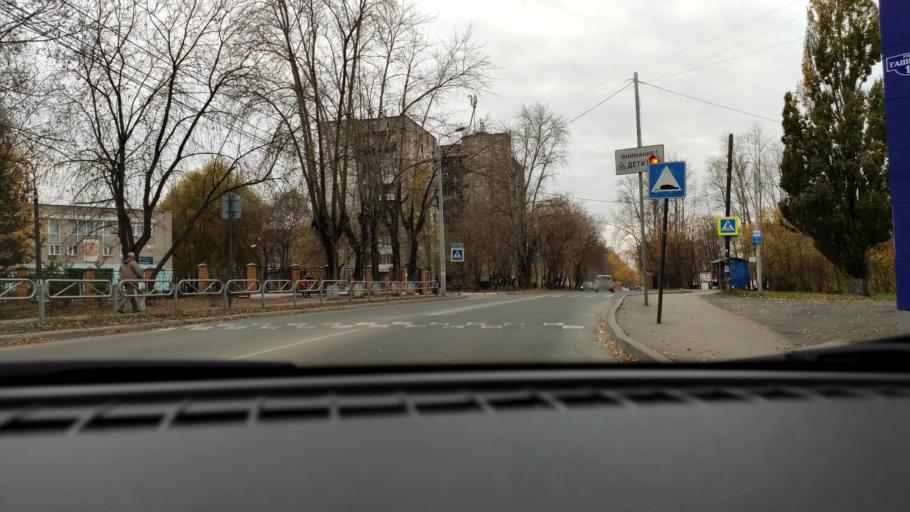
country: RU
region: Perm
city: Perm
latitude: 58.0670
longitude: 56.3564
